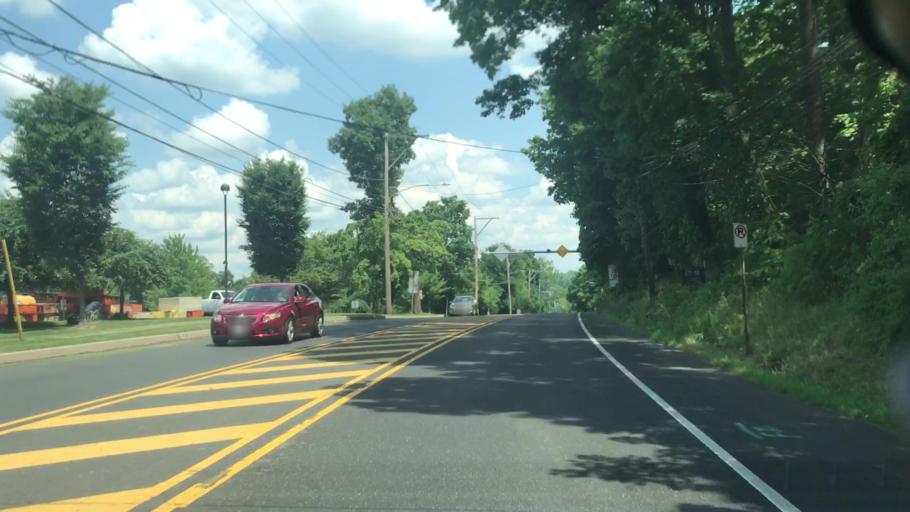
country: US
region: Pennsylvania
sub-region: Bucks County
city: New Hope
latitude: 40.3647
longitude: -74.9597
